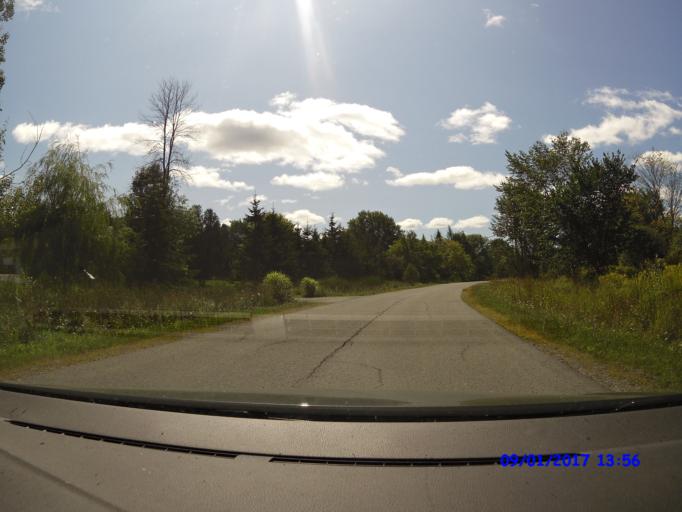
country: CA
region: Ontario
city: Bells Corners
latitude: 45.3603
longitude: -75.9557
